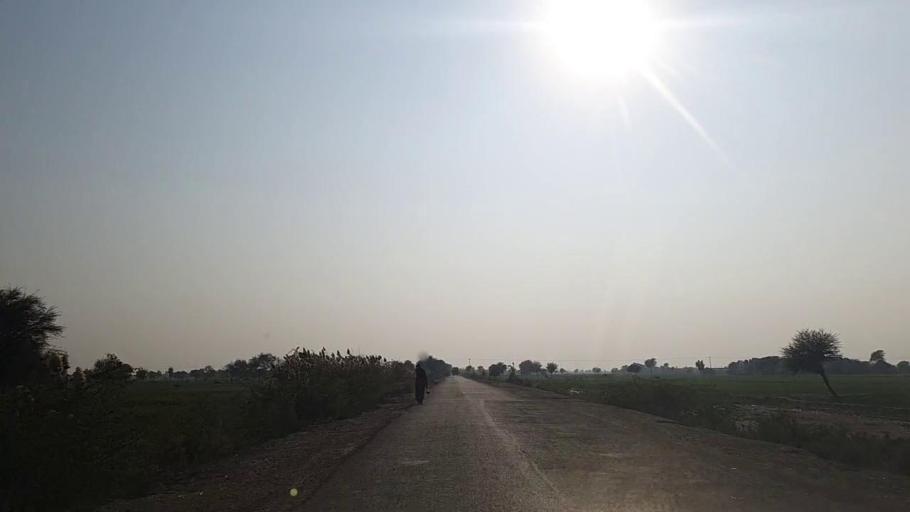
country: PK
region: Sindh
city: Jam Sahib
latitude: 26.2820
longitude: 68.6201
